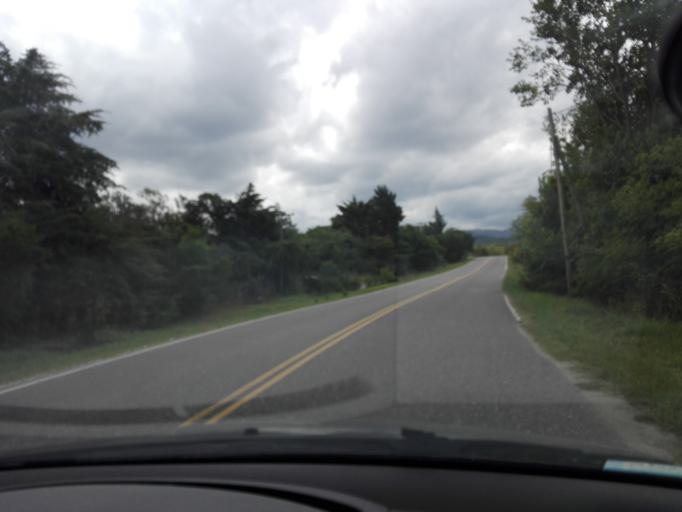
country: AR
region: Cordoba
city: Alta Gracia
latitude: -31.5890
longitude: -64.4680
